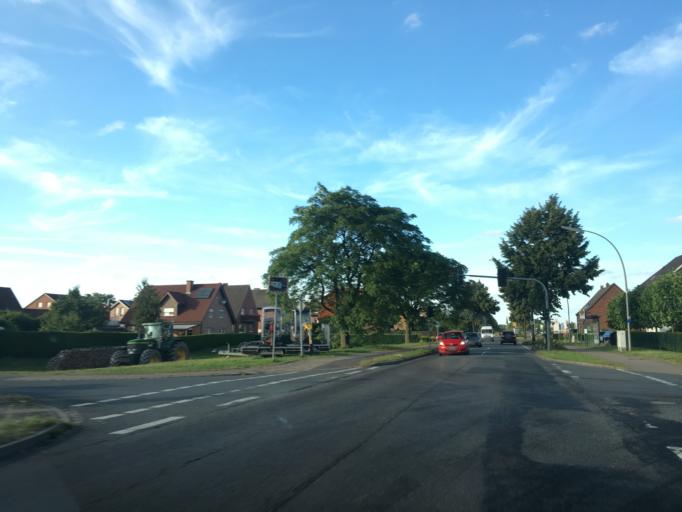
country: DE
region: North Rhine-Westphalia
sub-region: Regierungsbezirk Munster
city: Dulmen
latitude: 51.8110
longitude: 7.2500
